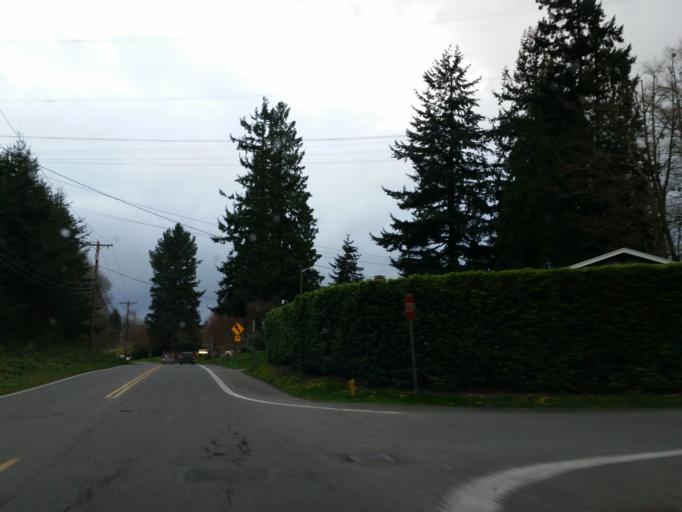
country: US
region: Washington
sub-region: Snohomish County
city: Alderwood Manor
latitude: 47.8090
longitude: -122.2754
